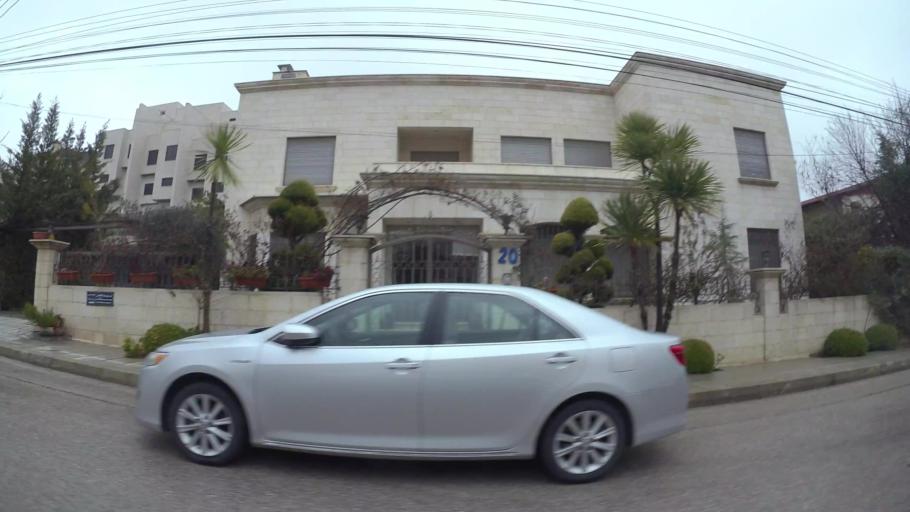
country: JO
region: Amman
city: Al Jubayhah
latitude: 32.0044
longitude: 35.8185
